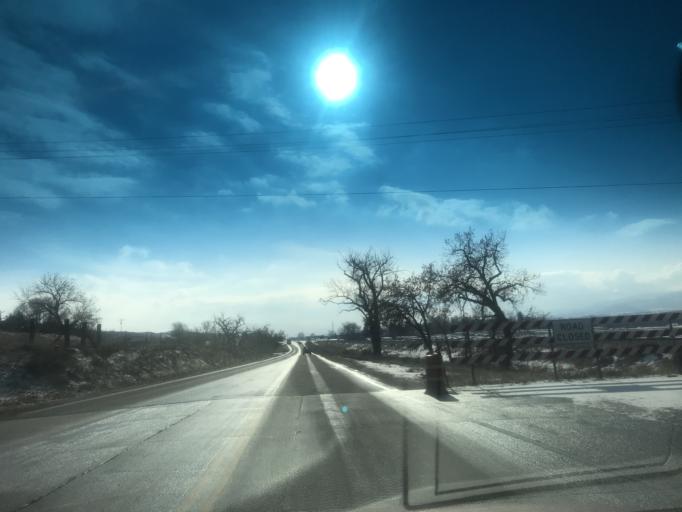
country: US
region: Colorado
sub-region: Douglas County
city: Highlands Ranch
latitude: 39.4858
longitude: -104.9956
